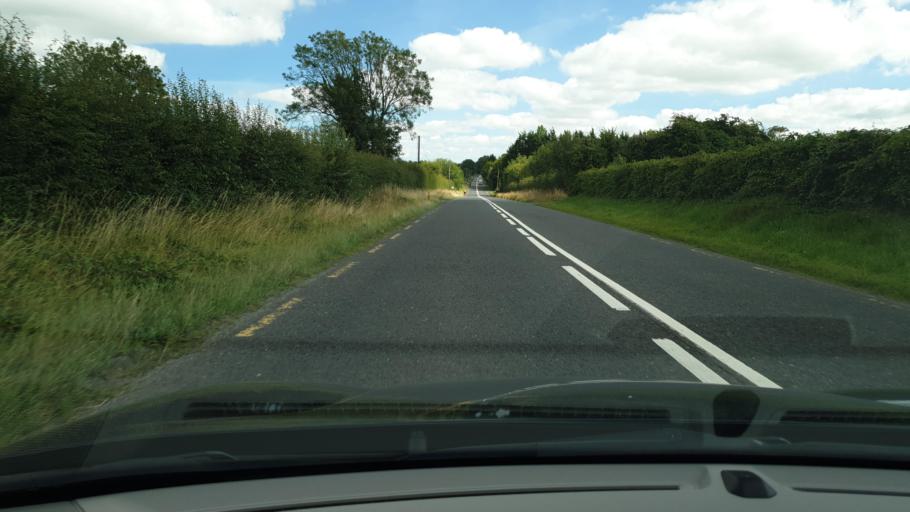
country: IE
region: Leinster
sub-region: An Mhi
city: Dunshaughlin
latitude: 53.5155
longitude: -6.6278
